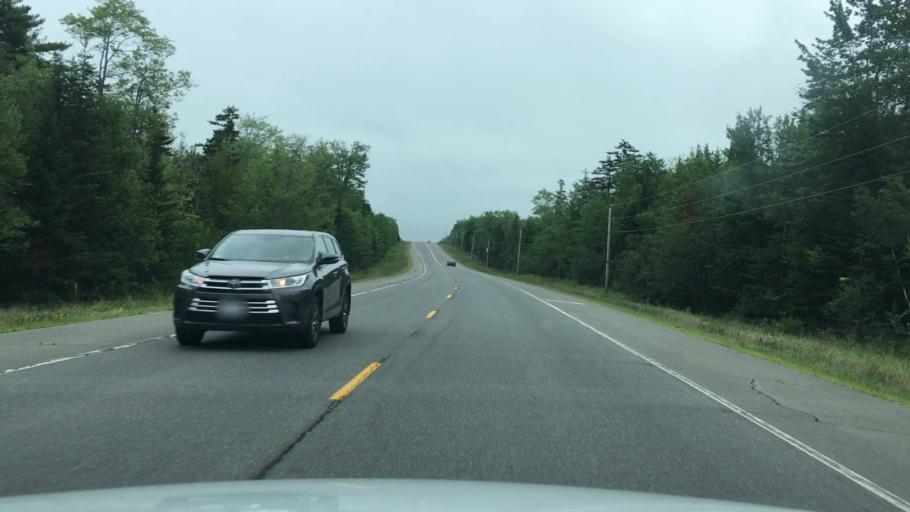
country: US
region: Maine
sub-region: Hancock County
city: Franklin
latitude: 44.8299
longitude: -68.1306
